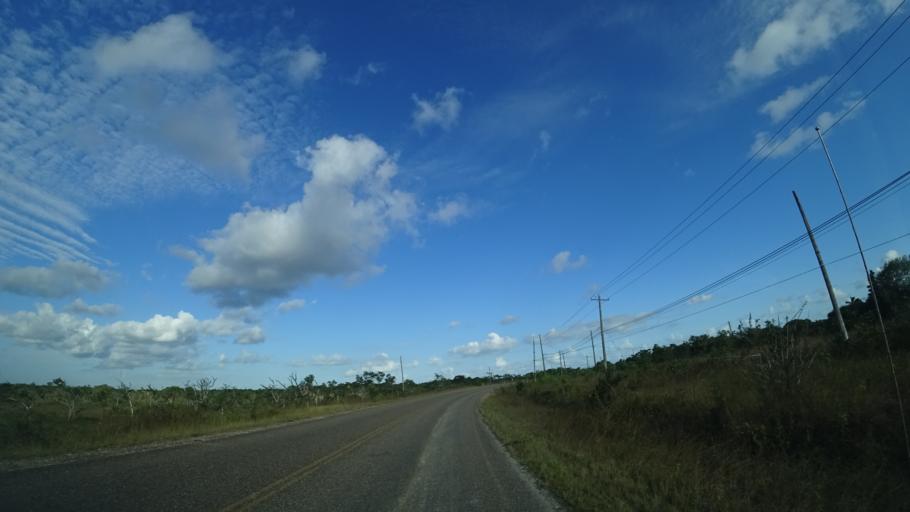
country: BZ
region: Belize
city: Belize City
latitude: 17.5812
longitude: -88.3754
